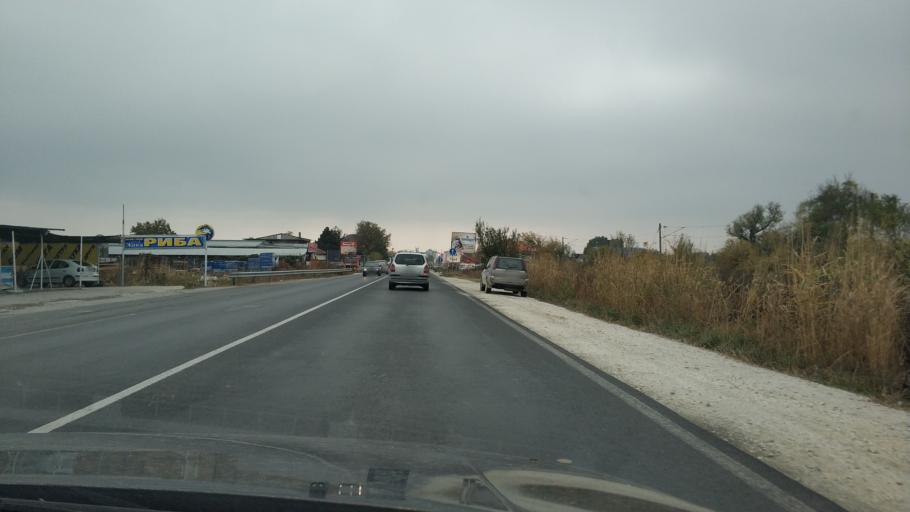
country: BG
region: Plovdiv
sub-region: Obshtina Plovdiv
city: Plovdiv
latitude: 42.2402
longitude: 24.7235
